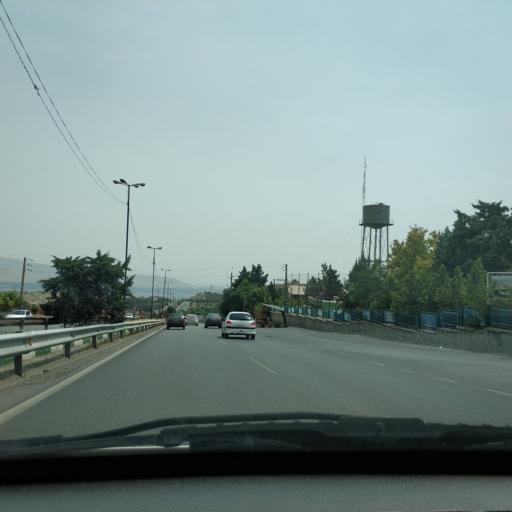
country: IR
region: Tehran
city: Tajrish
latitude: 35.7762
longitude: 51.5604
